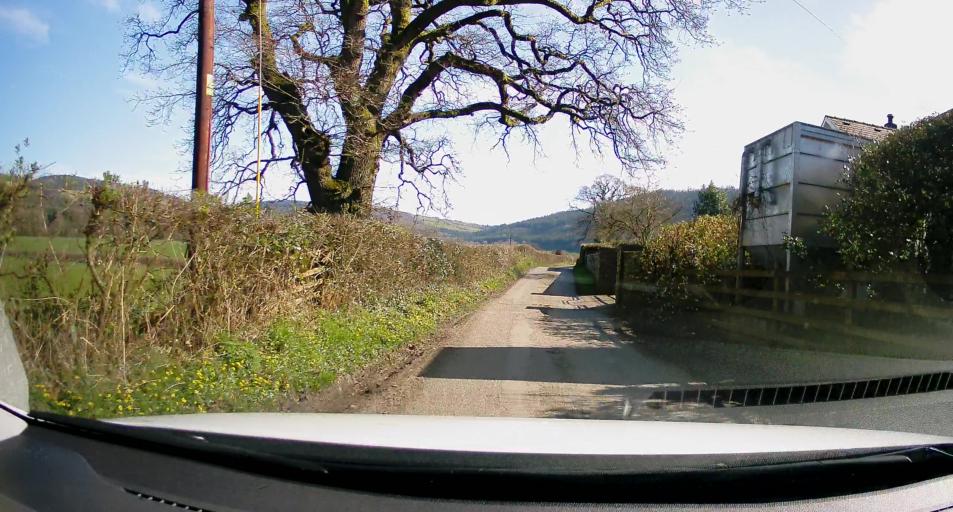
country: GB
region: Wales
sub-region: County of Ceredigion
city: Lledrod
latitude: 52.3320
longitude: -3.9564
